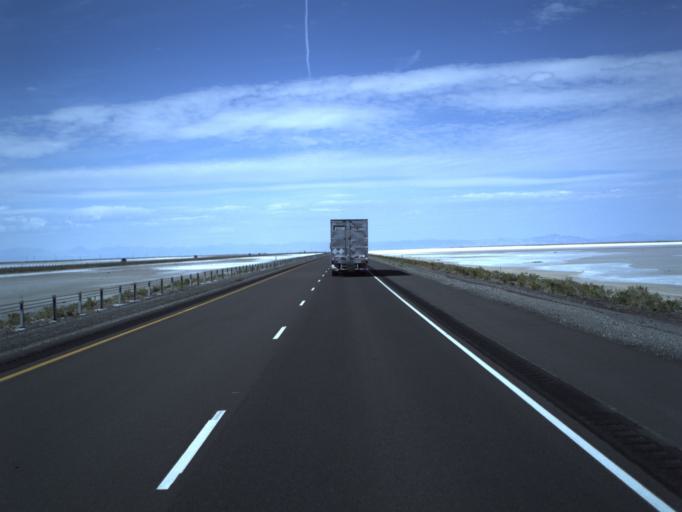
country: US
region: Utah
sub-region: Tooele County
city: Wendover
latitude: 40.7291
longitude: -113.3860
